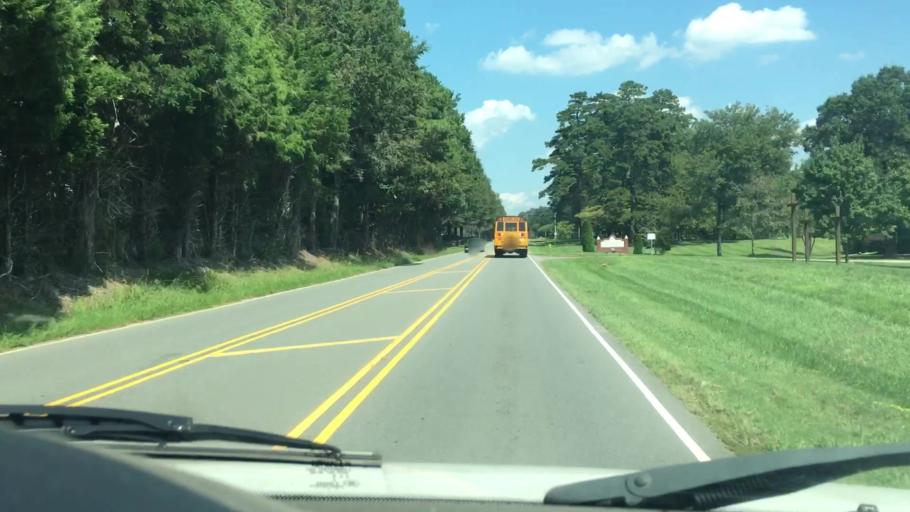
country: US
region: North Carolina
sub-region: Mecklenburg County
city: Huntersville
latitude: 35.3582
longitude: -80.8682
